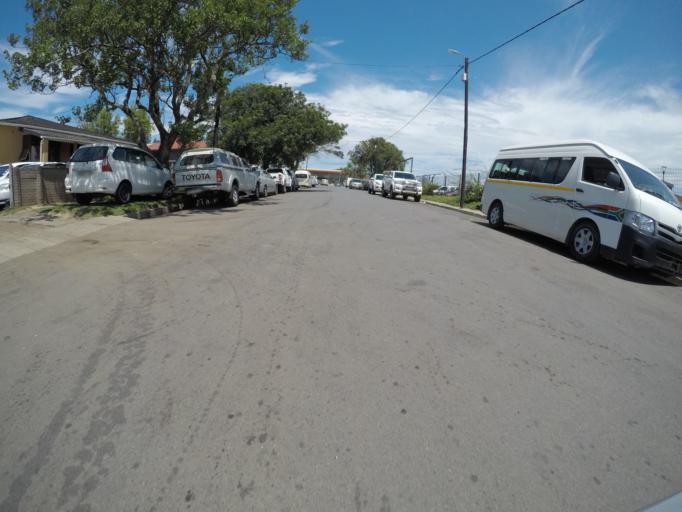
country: ZA
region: Eastern Cape
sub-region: Buffalo City Metropolitan Municipality
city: East London
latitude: -33.0345
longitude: 27.8551
